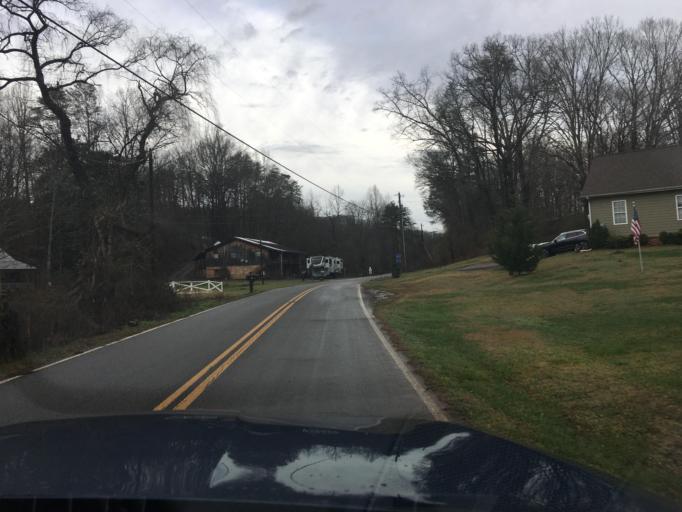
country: US
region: Tennessee
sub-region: McMinn County
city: Englewood
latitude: 35.3822
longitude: -84.4374
